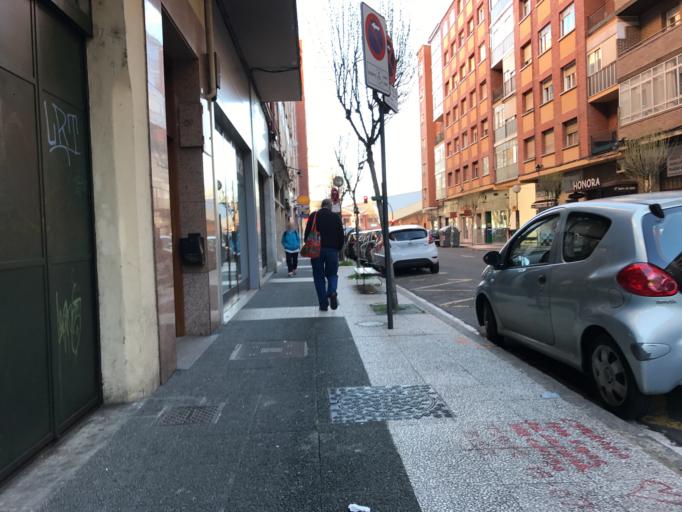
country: ES
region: Basque Country
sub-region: Provincia de Alava
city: Gasteiz / Vitoria
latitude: 42.8555
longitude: -2.6760
